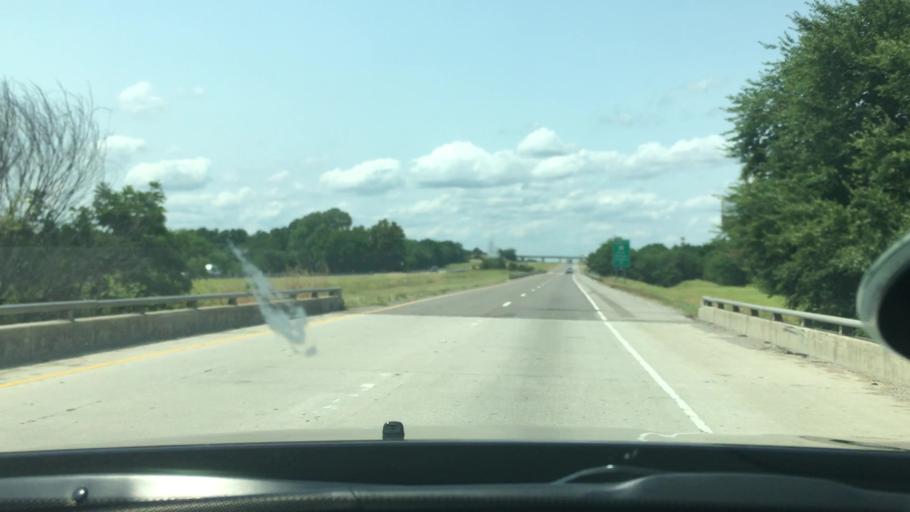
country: US
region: Oklahoma
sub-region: Murray County
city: Davis
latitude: 34.4986
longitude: -97.1687
